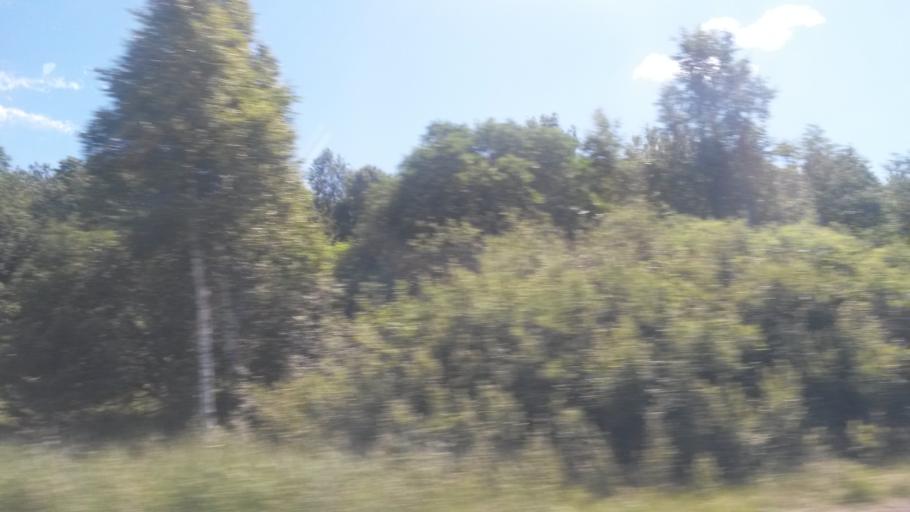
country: RU
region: Ivanovo
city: Rodniki
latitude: 57.0883
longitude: 41.6500
